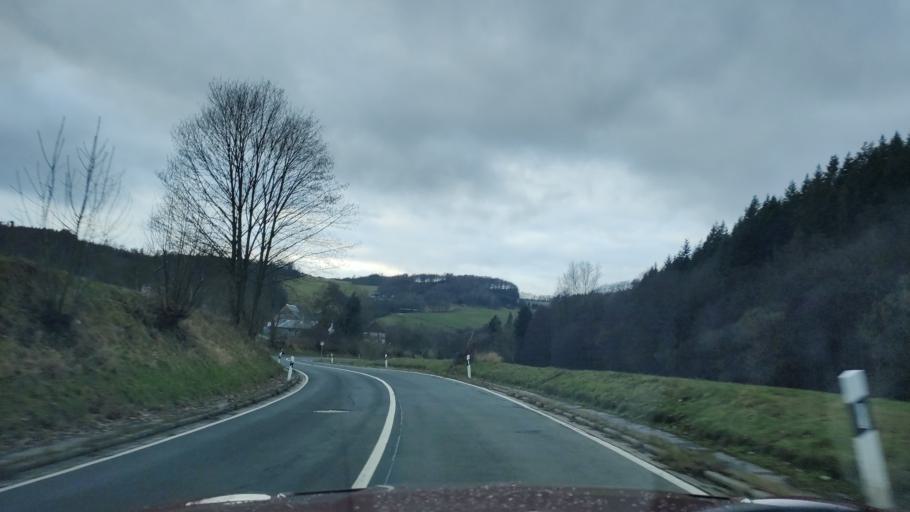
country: DE
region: North Rhine-Westphalia
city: Altena
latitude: 51.3294
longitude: 7.6866
